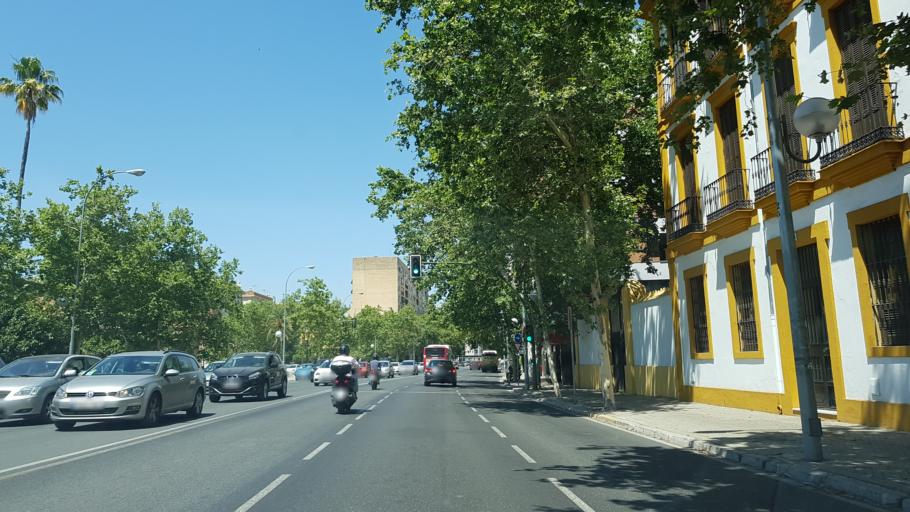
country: ES
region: Andalusia
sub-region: Provincia de Sevilla
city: Sevilla
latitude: 37.3762
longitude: -5.9846
